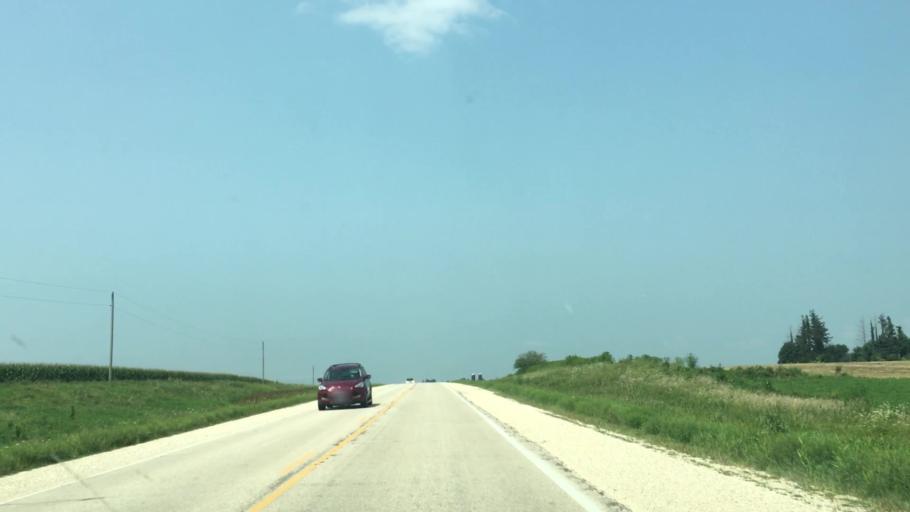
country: US
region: Iowa
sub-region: Fayette County
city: West Union
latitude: 42.9944
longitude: -91.8239
